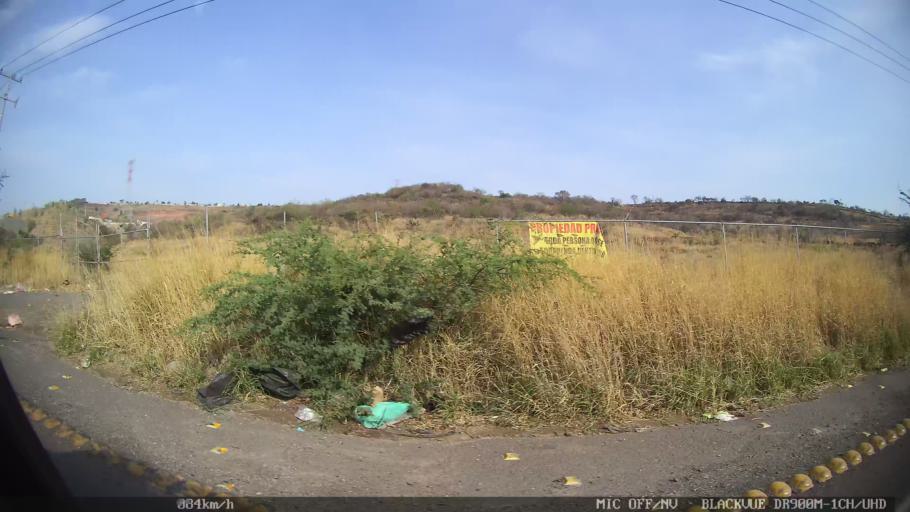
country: MX
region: Jalisco
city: Coyula
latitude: 20.6405
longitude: -103.2070
